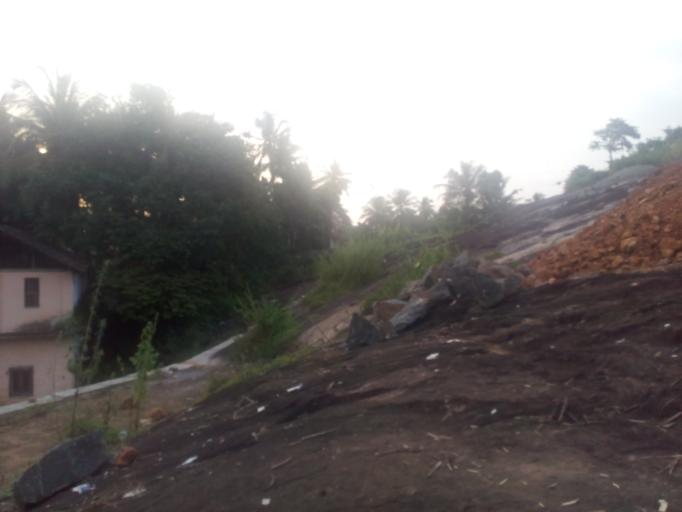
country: IN
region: Kerala
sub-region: Kozhikode
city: Mavoor
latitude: 11.2972
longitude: 75.9913
